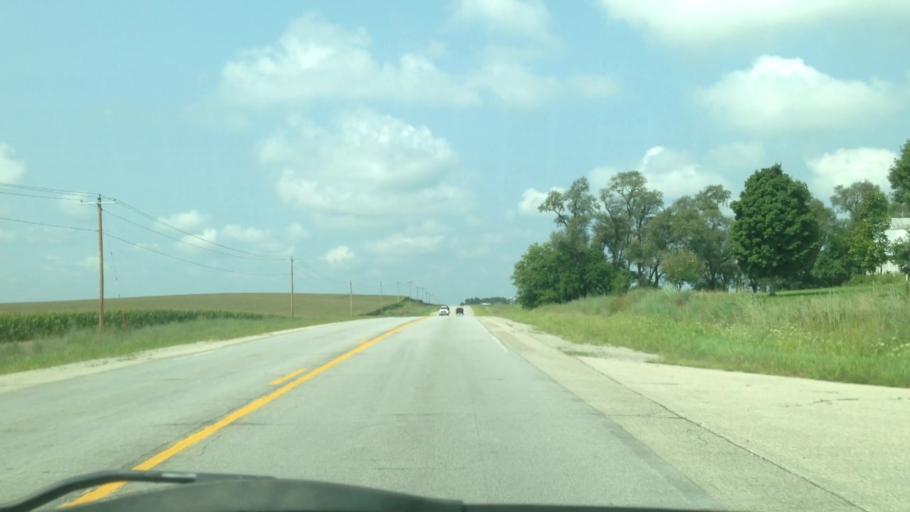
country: US
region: Iowa
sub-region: Benton County
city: Walford
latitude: 41.8762
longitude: -91.8509
